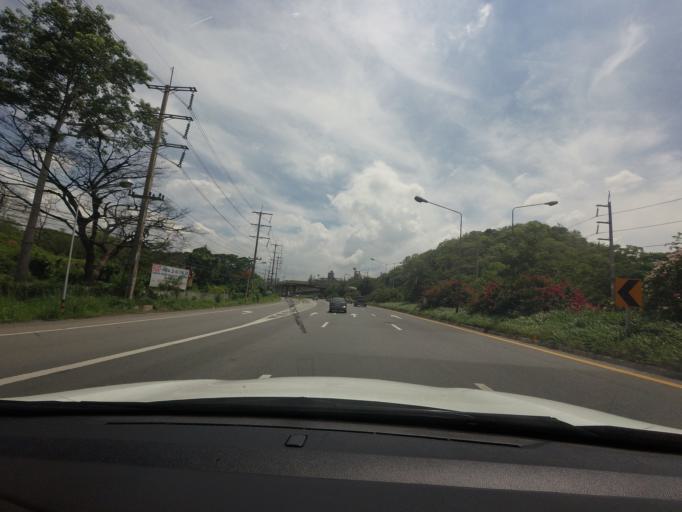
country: TH
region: Sara Buri
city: Muak Lek
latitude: 14.6331
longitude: 101.1062
